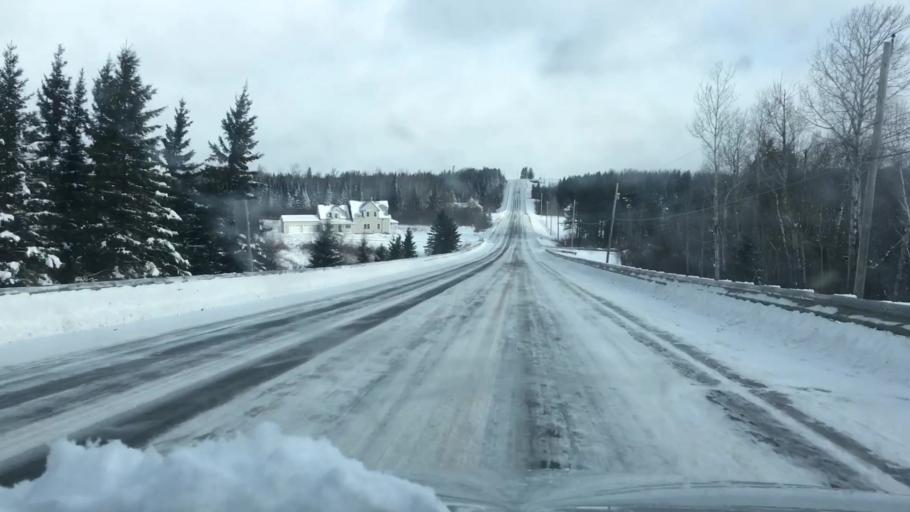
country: US
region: Maine
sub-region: Aroostook County
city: Van Buren
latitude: 47.0902
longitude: -67.9825
